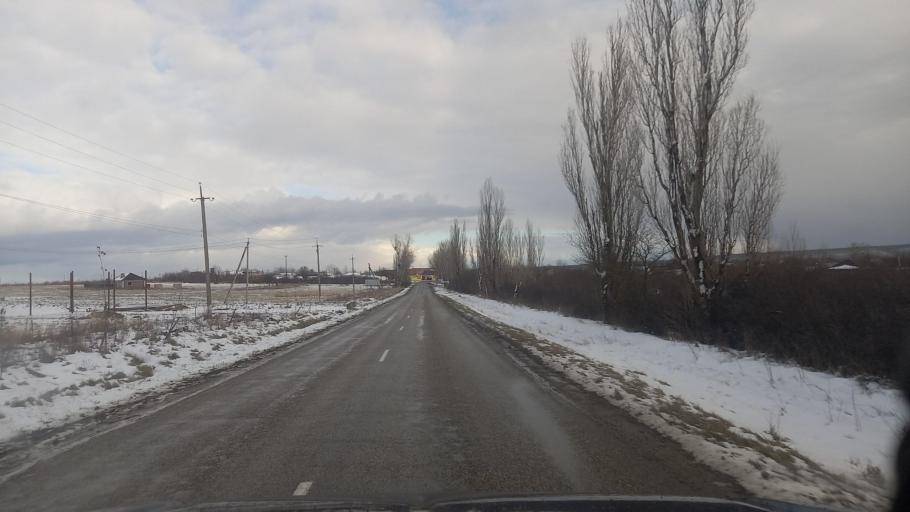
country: RU
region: Krasnodarskiy
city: Smolenskaya
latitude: 44.7749
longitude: 38.8286
